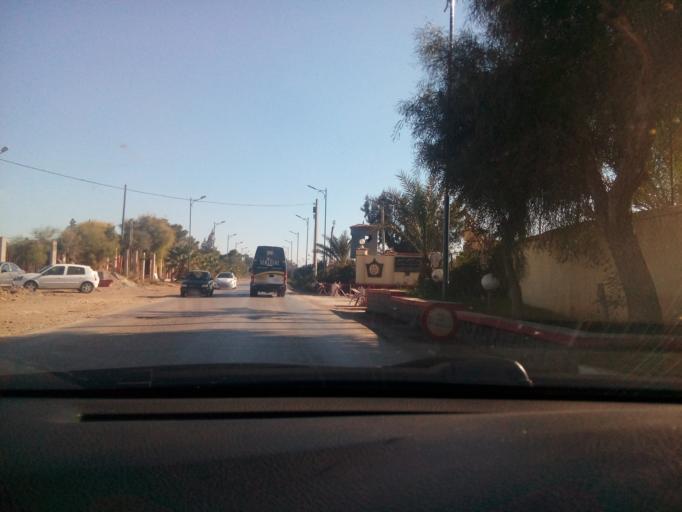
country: DZ
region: Oran
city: Es Senia
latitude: 35.6375
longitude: -0.6111
